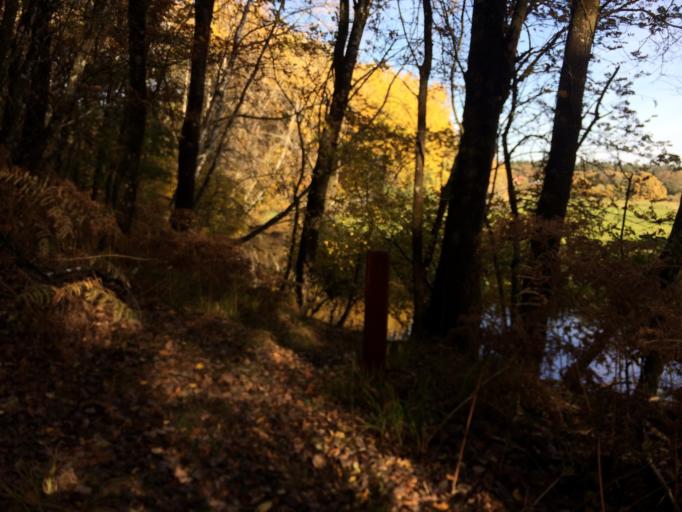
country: DK
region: Central Jutland
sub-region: Holstebro Kommune
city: Ulfborg
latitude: 56.2711
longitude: 8.4732
